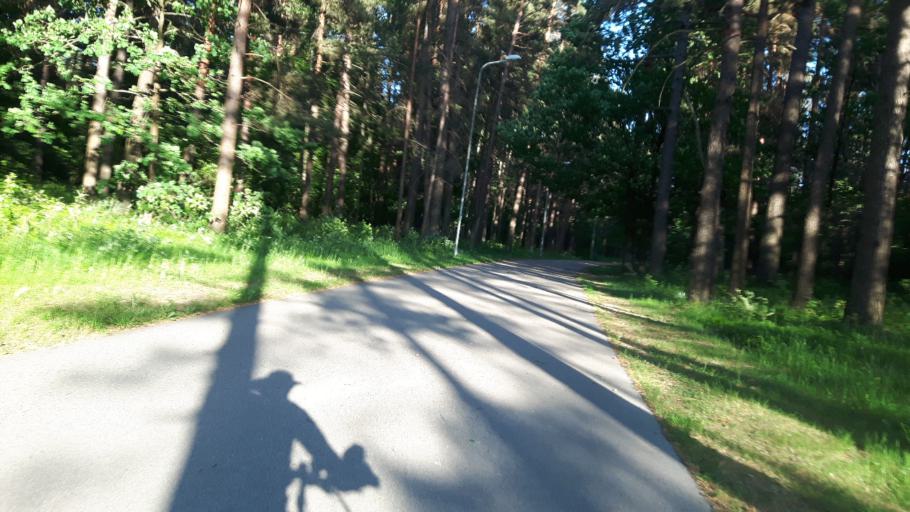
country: LV
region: Riga
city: Jaunciems
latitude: 57.0102
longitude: 24.1420
